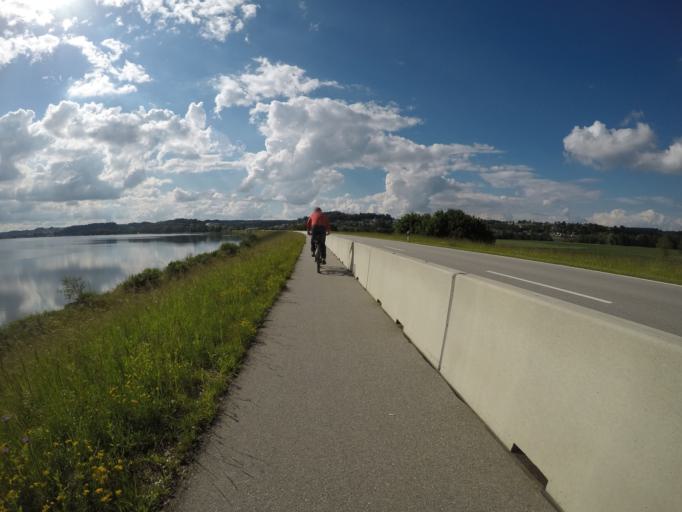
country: DE
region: Bavaria
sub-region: Lower Bavaria
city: Reisbach
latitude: 48.5672
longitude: 12.5957
